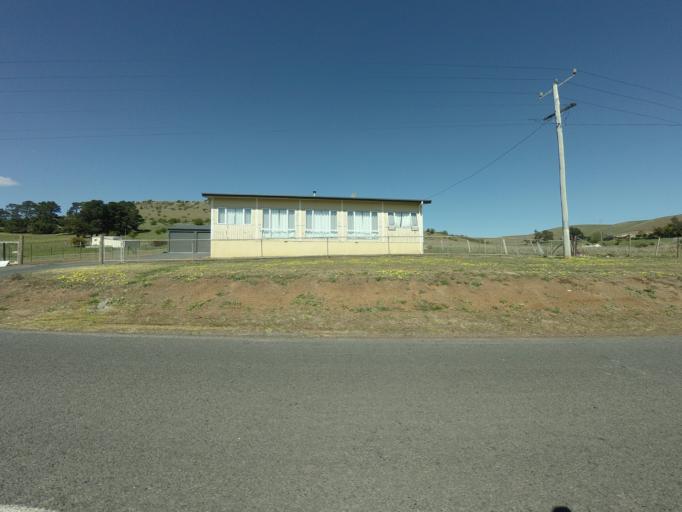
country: AU
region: Tasmania
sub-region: Derwent Valley
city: New Norfolk
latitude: -42.5617
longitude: 146.8297
